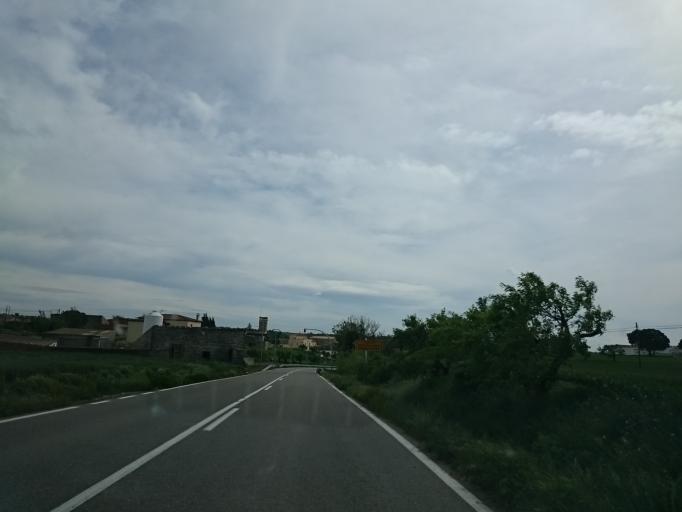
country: ES
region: Catalonia
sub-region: Provincia de Lleida
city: Ivorra
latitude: 41.7451
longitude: 1.3850
